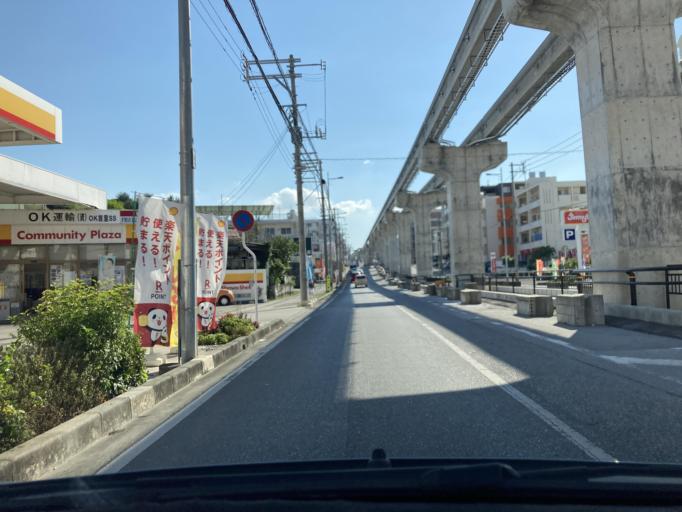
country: JP
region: Okinawa
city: Naha-shi
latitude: 26.2254
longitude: 127.7285
